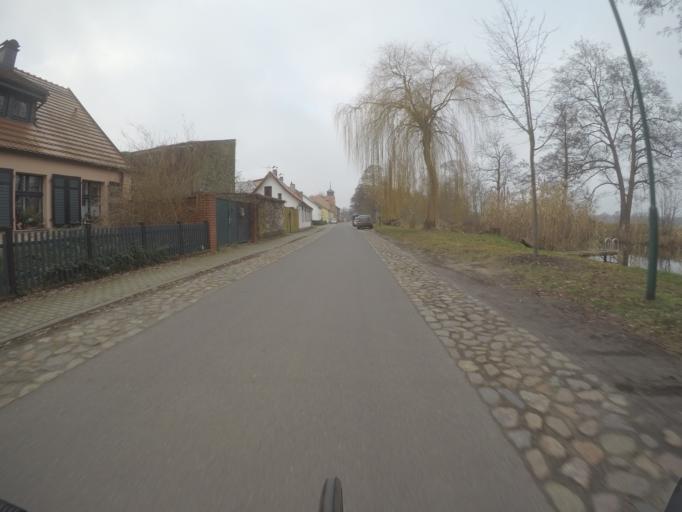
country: DE
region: Brandenburg
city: Marienwerder
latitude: 52.8562
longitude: 13.5120
